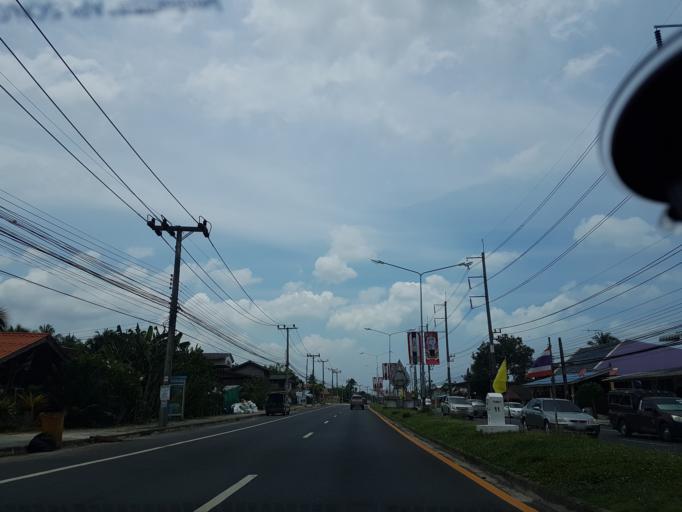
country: TH
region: Songkhla
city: Songkhla
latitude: 7.1063
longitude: 100.6329
